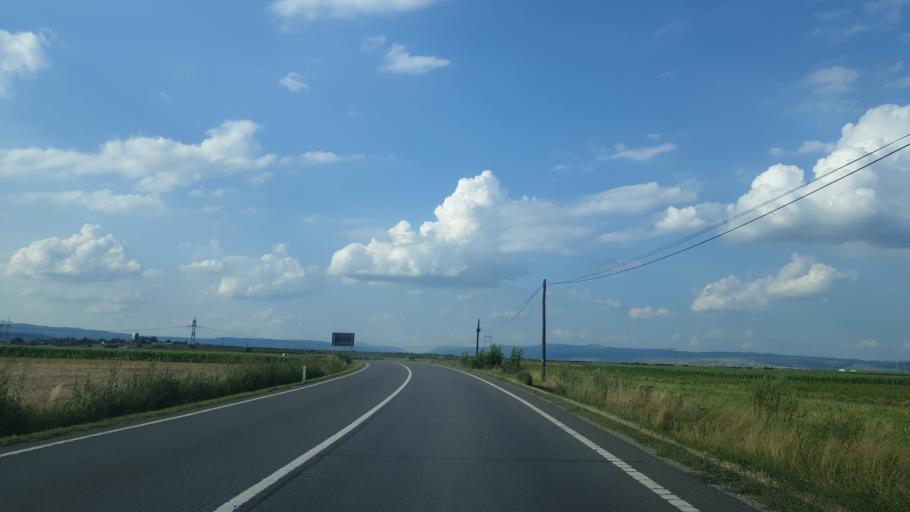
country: RO
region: Covasna
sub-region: Comuna Chichis
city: Chichis
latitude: 45.7994
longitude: 25.8048
